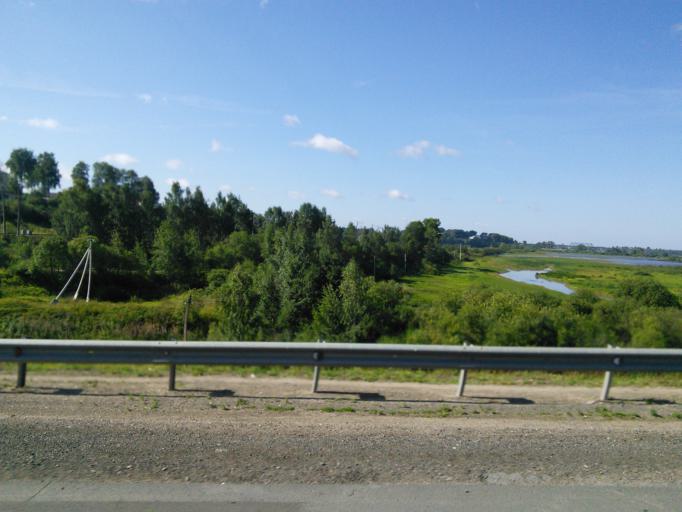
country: RU
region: Vologda
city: Sheksna
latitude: 59.2107
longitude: 38.4984
